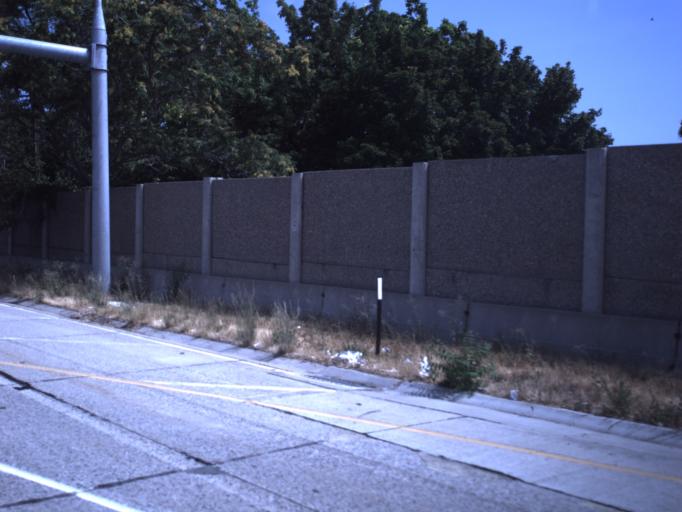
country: US
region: Utah
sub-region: Salt Lake County
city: West Valley City
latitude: 40.6835
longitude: -111.9815
